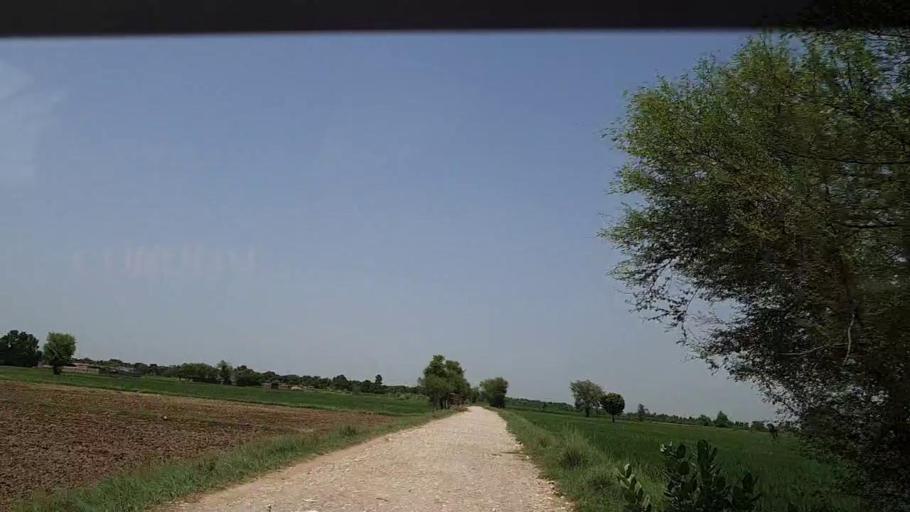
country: PK
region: Sindh
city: Tharu Shah
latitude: 26.9577
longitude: 68.0434
